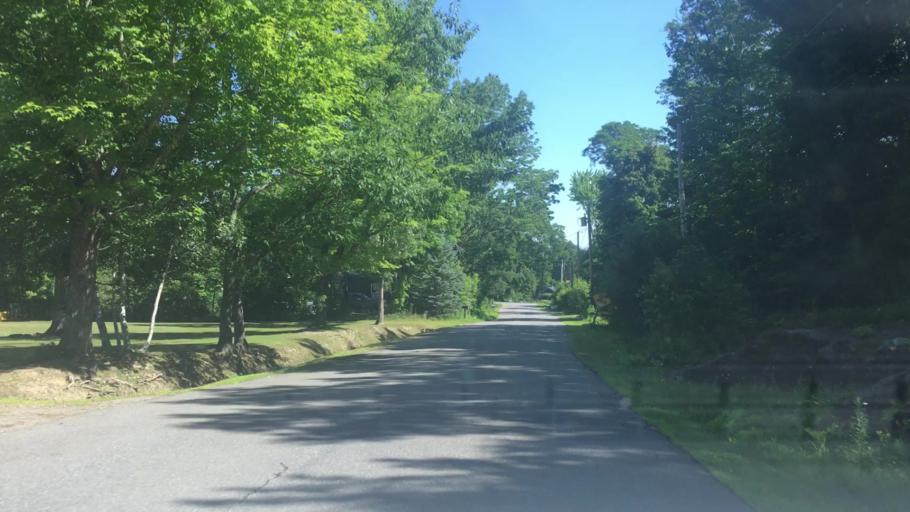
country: US
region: Maine
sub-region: Waldo County
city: Northport
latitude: 44.3806
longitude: -68.9812
